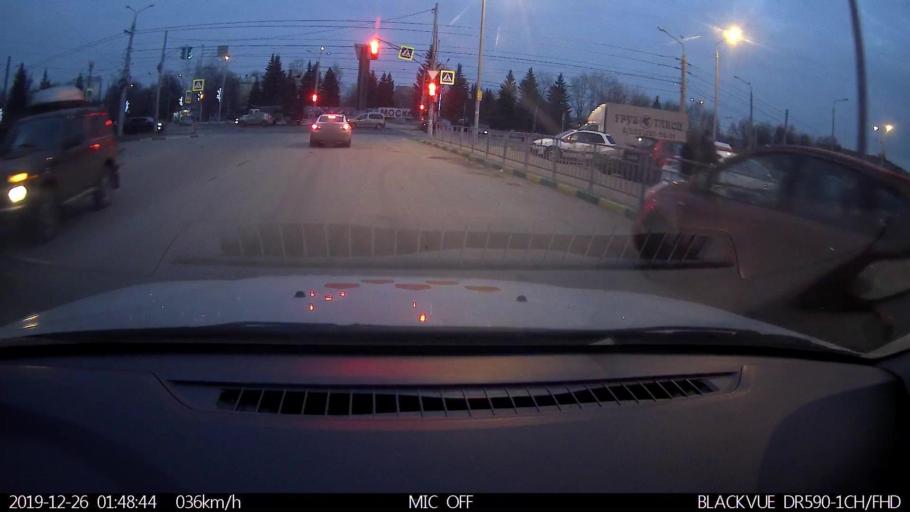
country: RU
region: Nizjnij Novgorod
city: Nizhniy Novgorod
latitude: 56.3234
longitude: 43.8809
